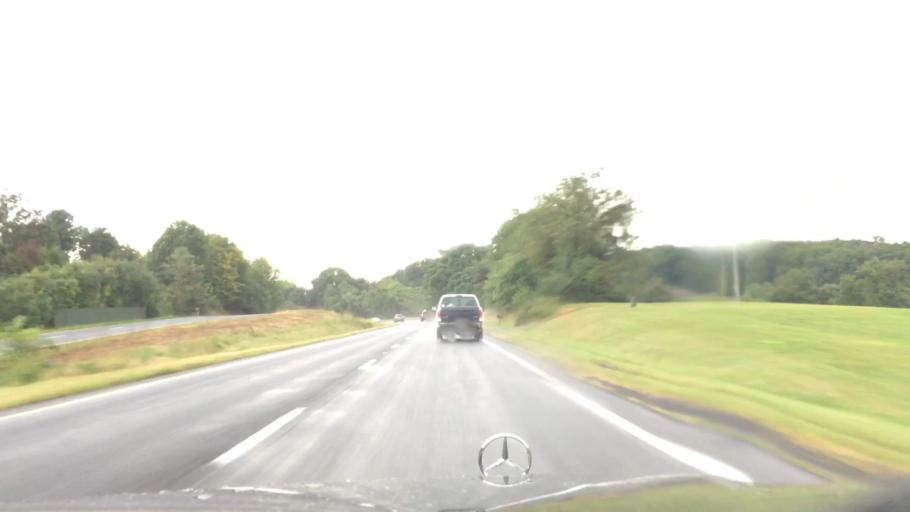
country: US
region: Virginia
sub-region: City of Winchester
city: Winchester
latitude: 39.2589
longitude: -78.2199
